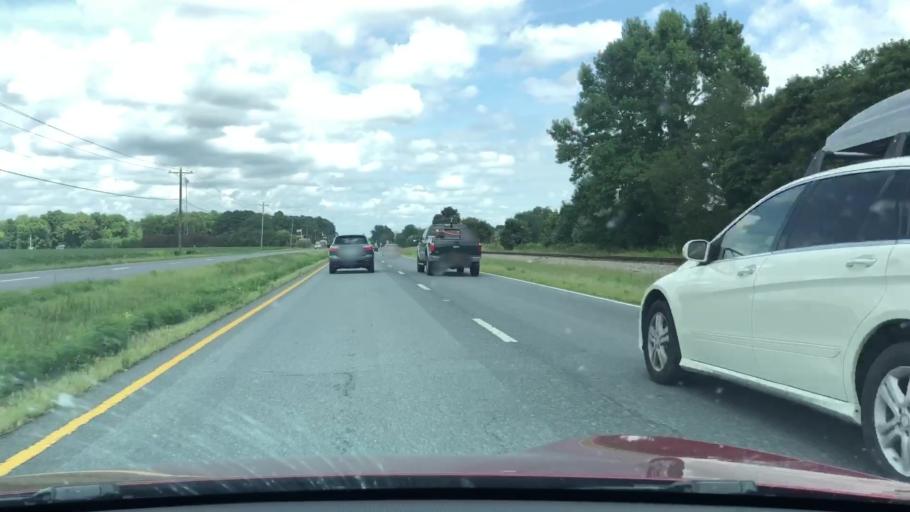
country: US
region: Virginia
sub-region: Accomack County
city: Onancock
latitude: 37.6615
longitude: -75.7347
